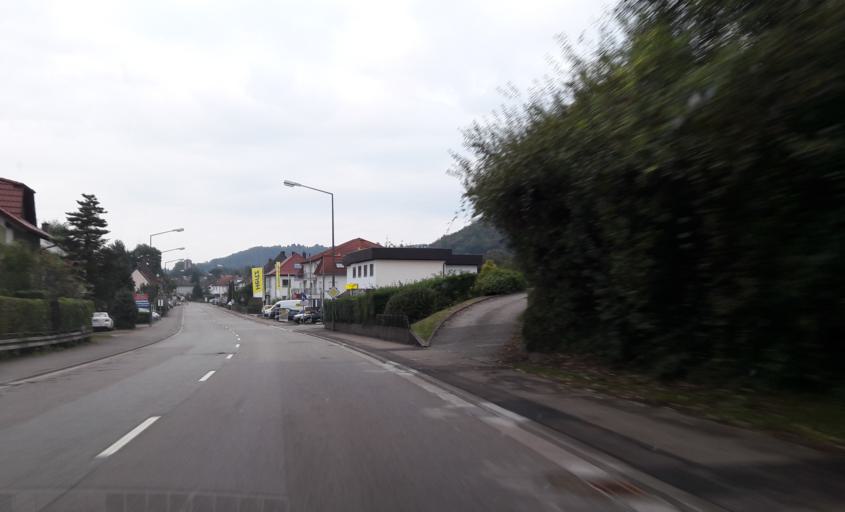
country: DE
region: Saarland
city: Homburg
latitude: 49.2781
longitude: 7.3146
